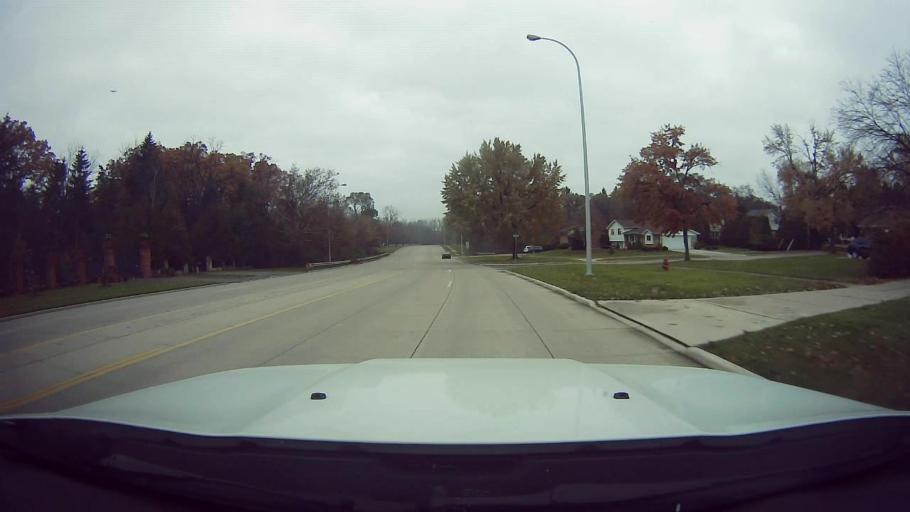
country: US
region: Michigan
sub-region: Wayne County
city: Dearborn Heights
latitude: 42.3333
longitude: -83.2613
